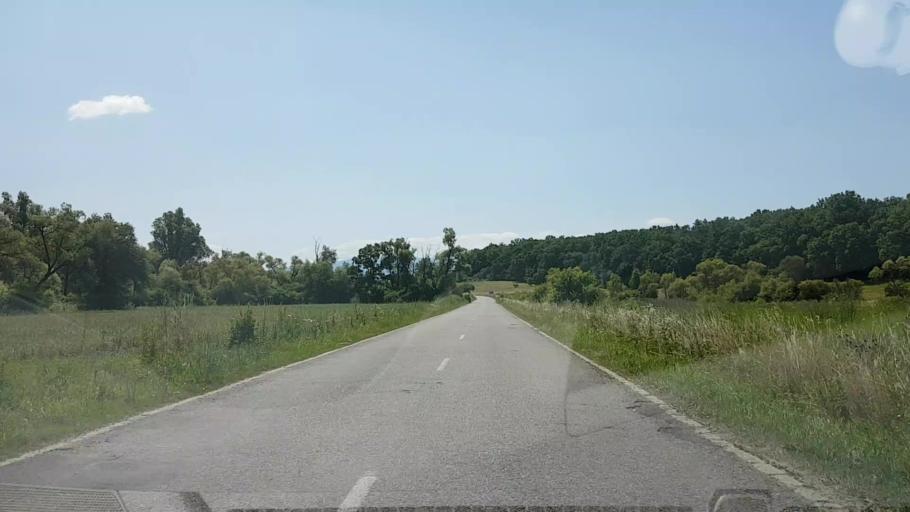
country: RO
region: Brasov
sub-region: Comuna Cincu
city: Cincu
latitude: 45.8740
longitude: 24.8197
